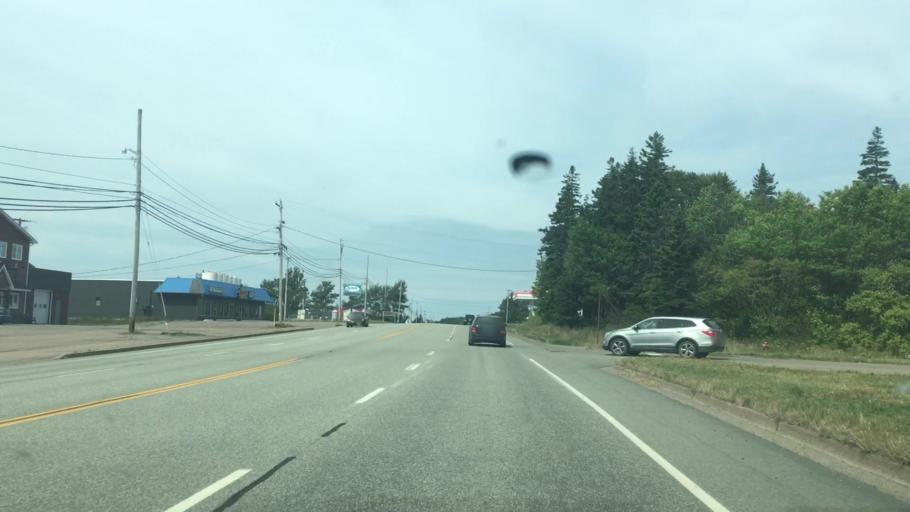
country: CA
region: Nova Scotia
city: Port Hawkesbury
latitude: 45.6397
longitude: -61.3856
